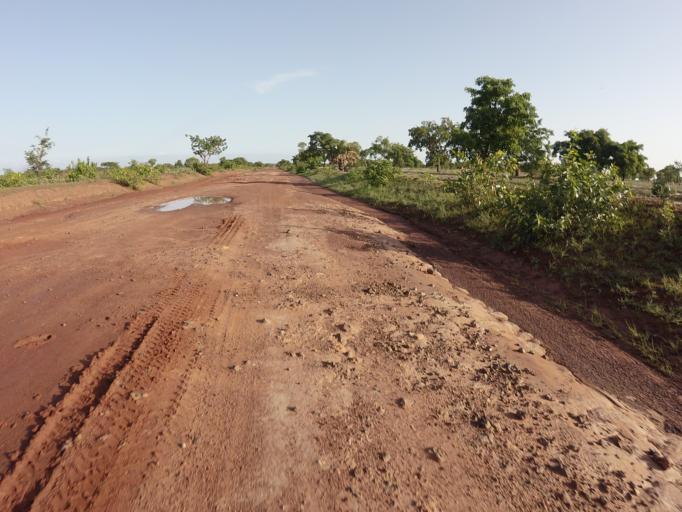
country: TG
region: Savanes
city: Sansanne-Mango
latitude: 10.3786
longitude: -0.0946
